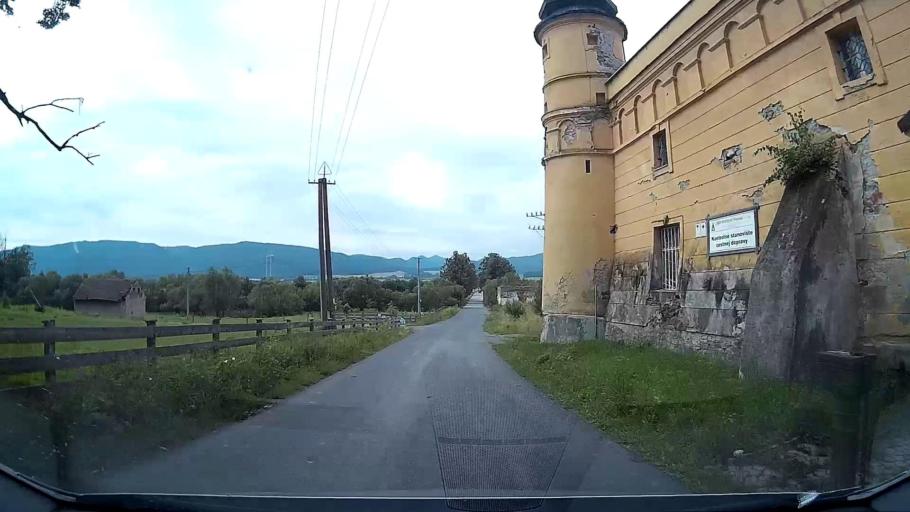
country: SK
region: Presovsky
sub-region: Okres Poprad
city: Poprad
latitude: 48.9886
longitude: 20.3809
